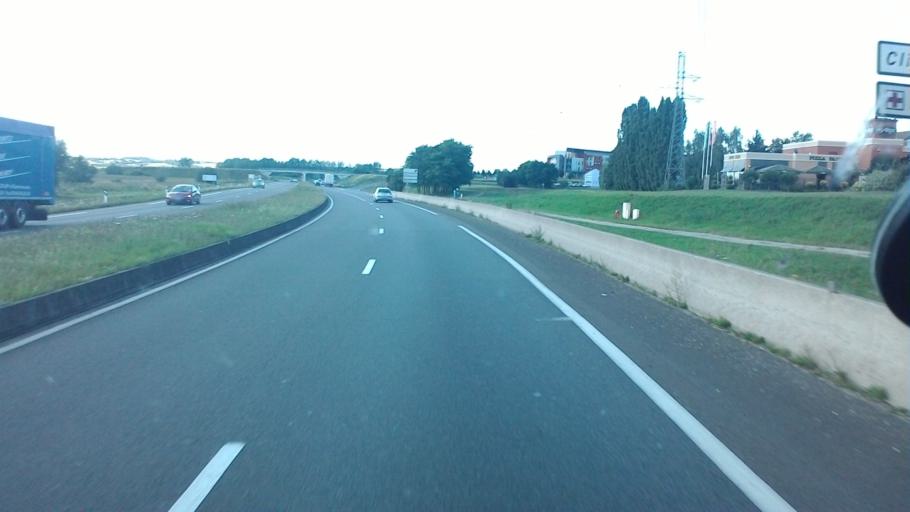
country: FR
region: Franche-Comte
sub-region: Departement de la Haute-Saone
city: Noidans-les-Vesoul
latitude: 47.6315
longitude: 6.1383
